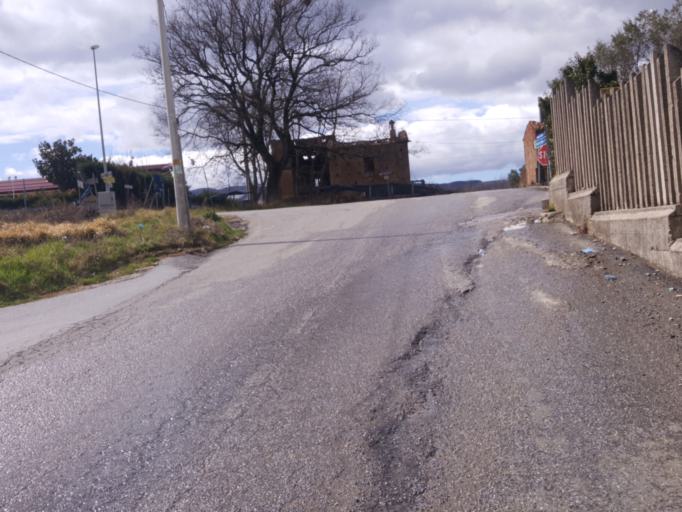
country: IT
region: Calabria
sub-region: Provincia di Cosenza
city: Piane Crati
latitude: 39.2194
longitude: 16.3067
